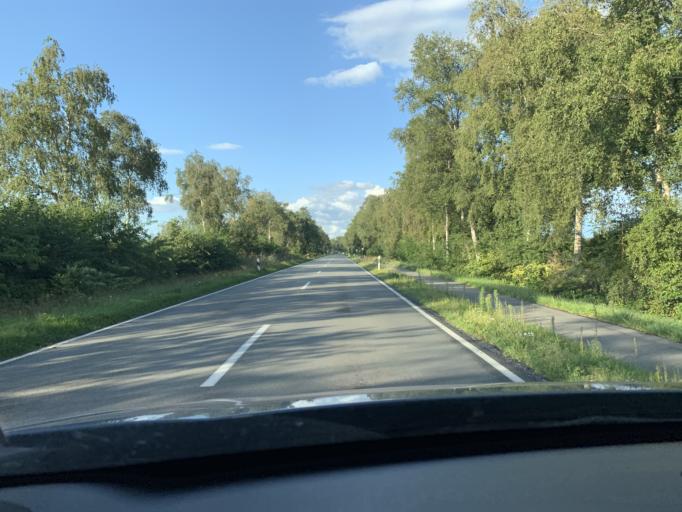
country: DE
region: Lower Saxony
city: Edewecht
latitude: 53.0947
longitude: 7.9463
